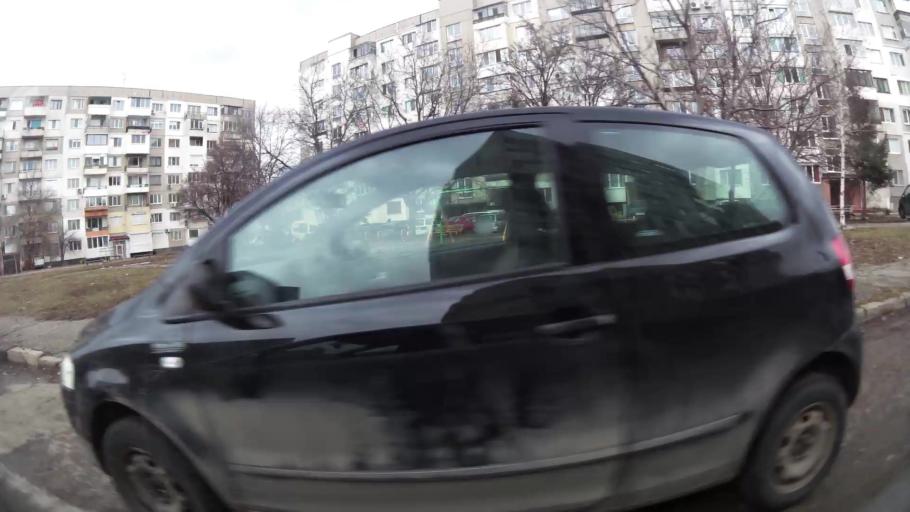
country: BG
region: Sofia-Capital
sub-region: Stolichna Obshtina
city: Sofia
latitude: 42.7329
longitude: 23.2871
